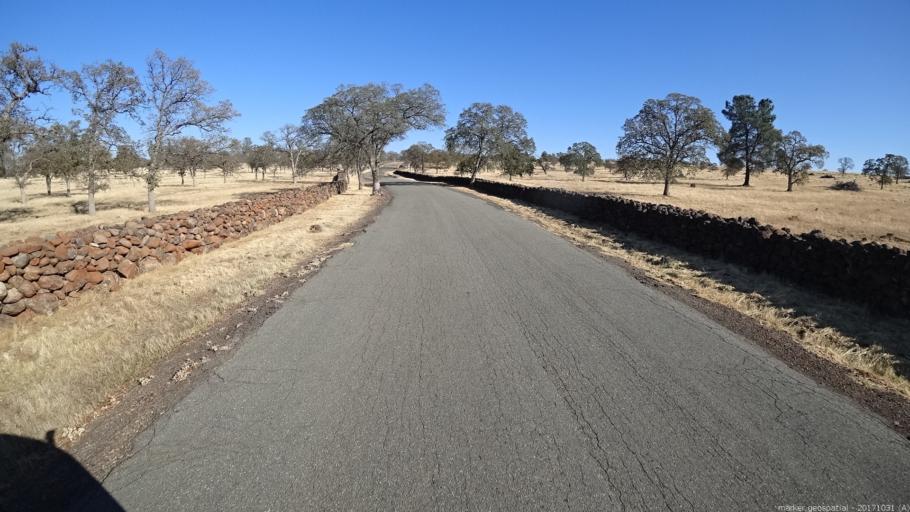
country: US
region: California
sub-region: Shasta County
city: Palo Cedro
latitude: 40.4624
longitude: -122.0829
